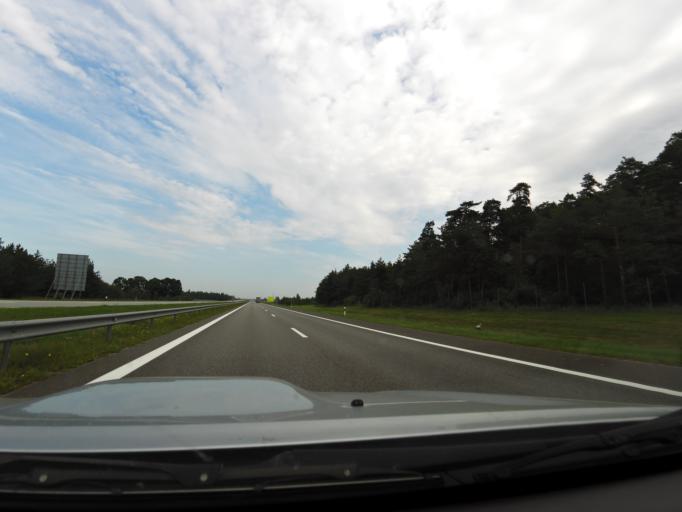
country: LT
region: Vilnius County
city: Ukmerge
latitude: 55.2789
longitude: 24.8067
